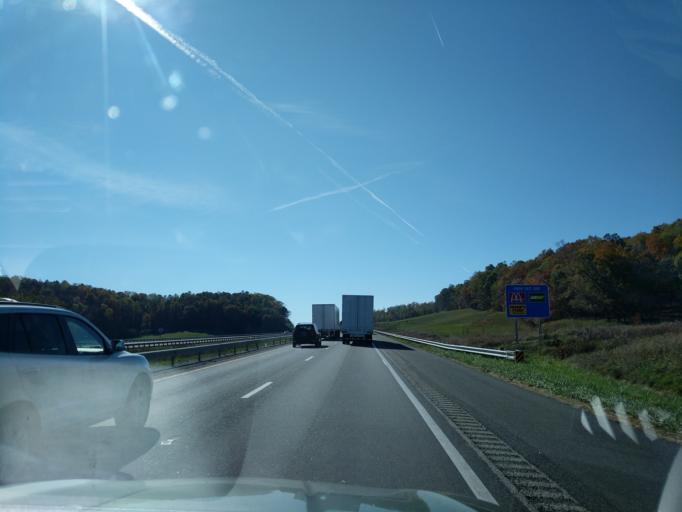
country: US
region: Virginia
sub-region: City of Buena Vista
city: Buena Vista
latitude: 37.9035
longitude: -79.2665
